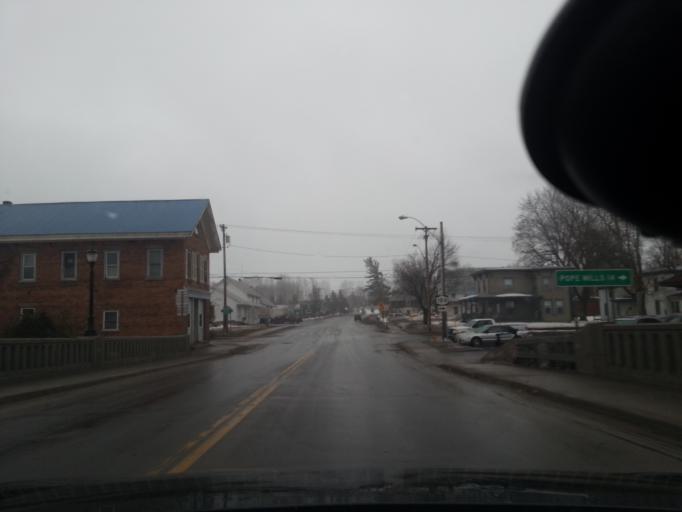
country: US
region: New York
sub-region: St. Lawrence County
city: Ogdensburg
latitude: 44.6167
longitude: -75.4052
